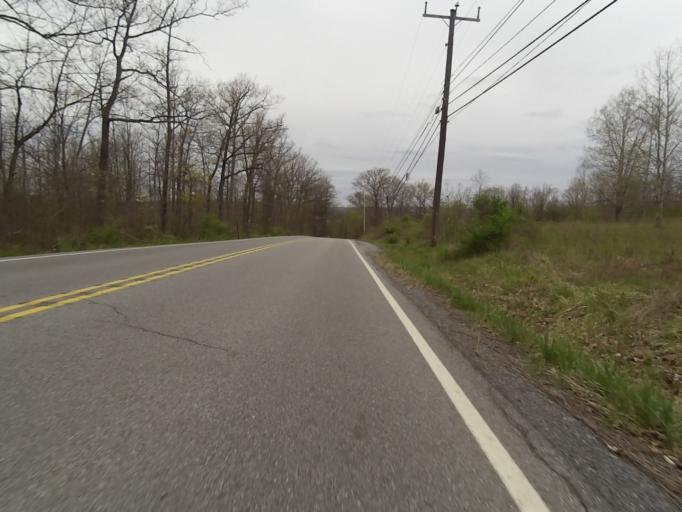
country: US
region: Pennsylvania
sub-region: Clearfield County
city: Troy
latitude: 40.9029
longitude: -78.1888
